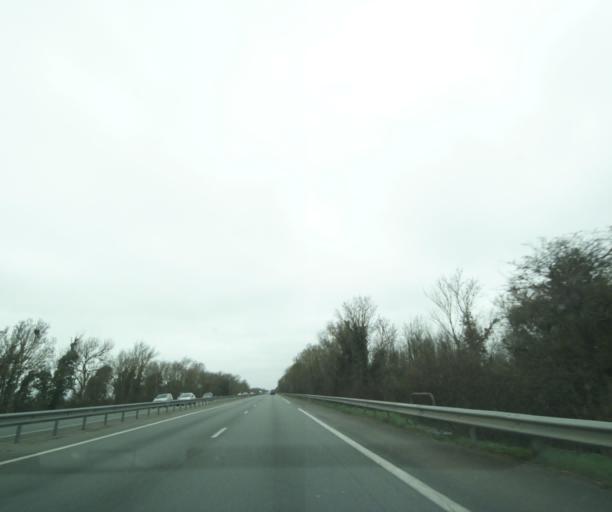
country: FR
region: Poitou-Charentes
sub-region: Departement de la Charente-Maritime
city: Chatelaillon-Plage
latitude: 46.0864
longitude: -1.0810
